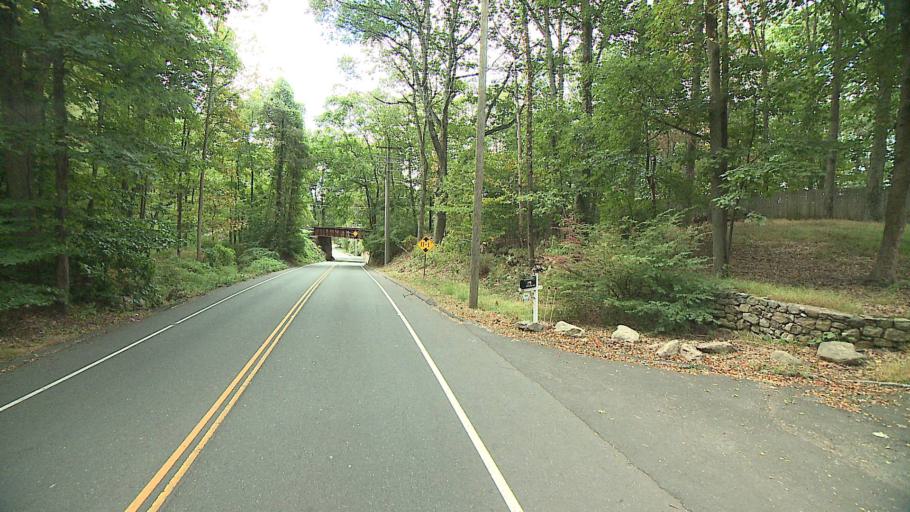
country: US
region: Connecticut
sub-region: Fairfield County
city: New Canaan
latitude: 41.1232
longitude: -73.4979
